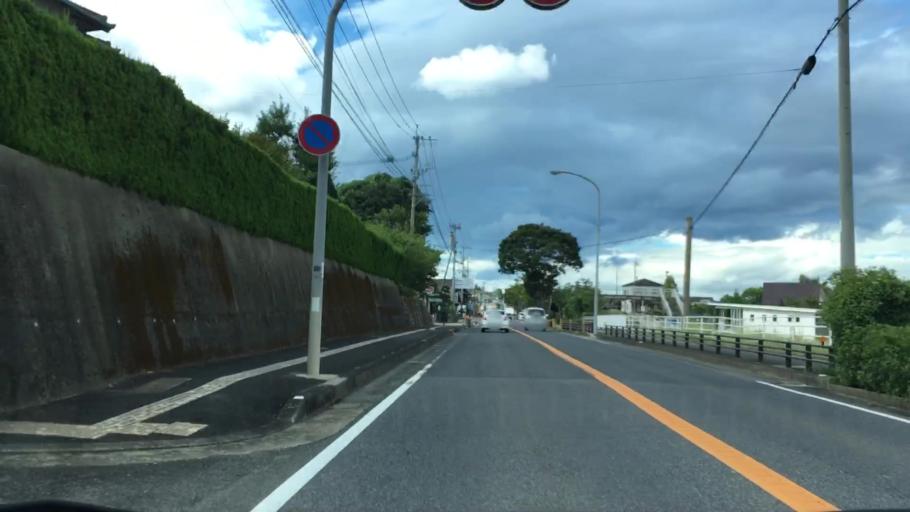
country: JP
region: Saga Prefecture
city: Imaricho-ko
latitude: 33.2080
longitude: 129.8502
